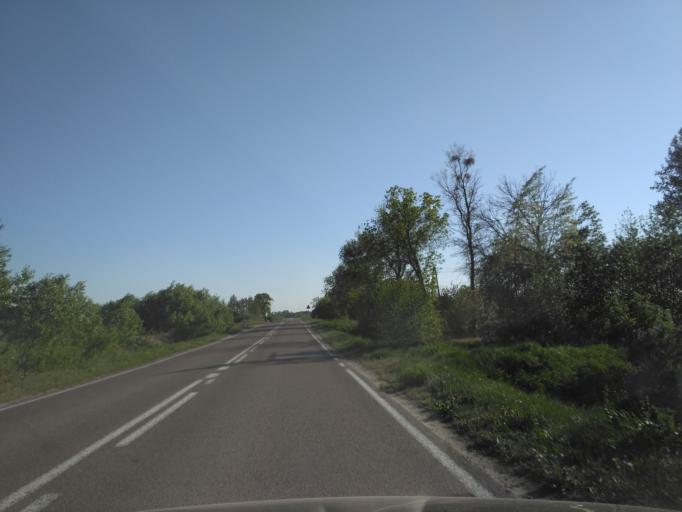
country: PL
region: Lublin Voivodeship
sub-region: Powiat swidnicki
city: Trawniki
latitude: 51.2025
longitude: 23.0663
